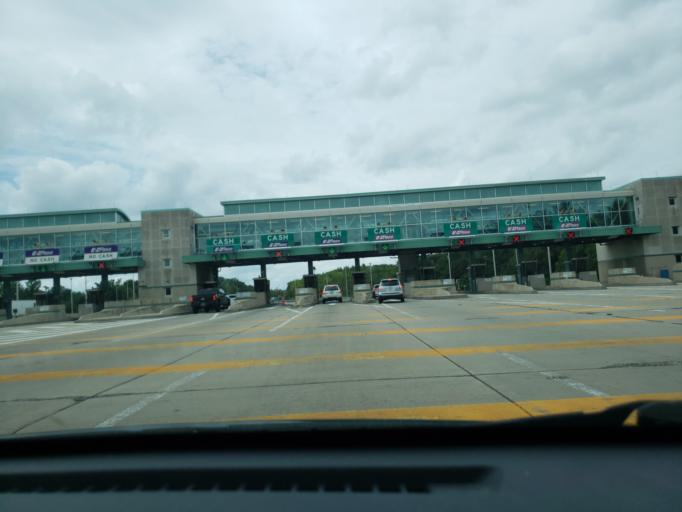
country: US
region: New Jersey
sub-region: Salem County
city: Carneys Point
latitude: 39.6866
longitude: -75.4474
